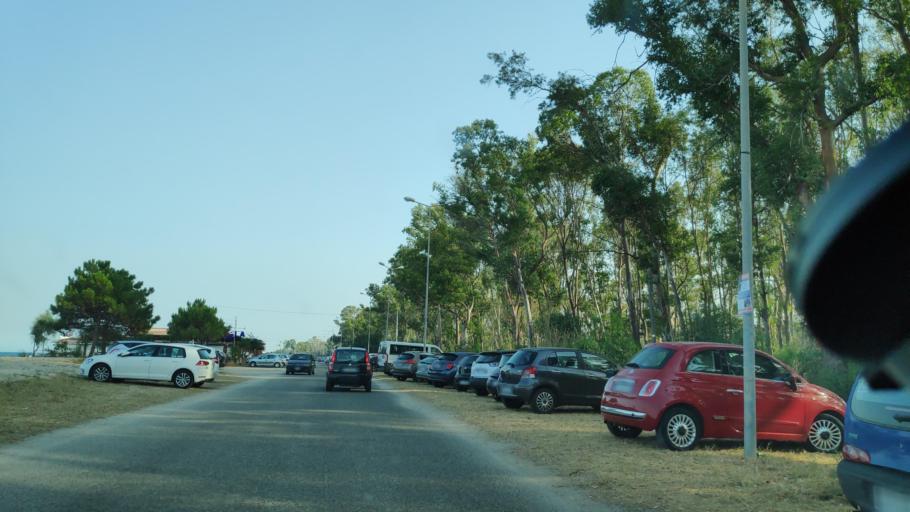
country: IT
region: Calabria
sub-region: Provincia di Catanzaro
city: Sant'Andrea Ionio Marina
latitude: 38.6155
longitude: 16.5609
